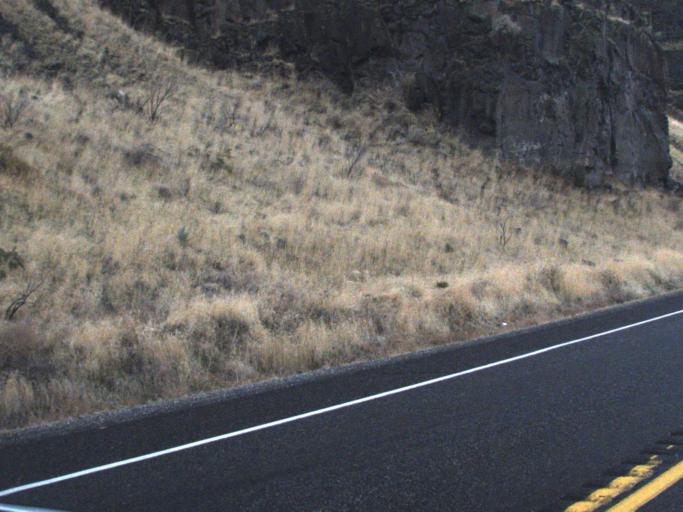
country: US
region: Washington
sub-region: Benton County
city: Finley
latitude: 46.0522
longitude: -118.9356
